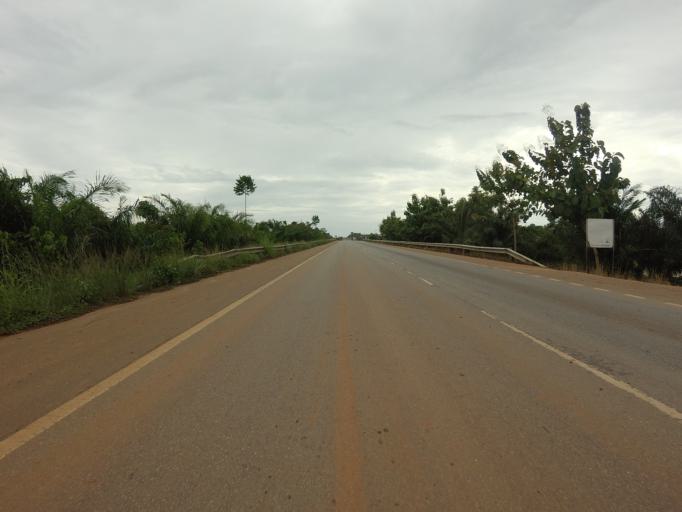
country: GH
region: Eastern
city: Nkawkaw
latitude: 6.5297
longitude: -0.7555
